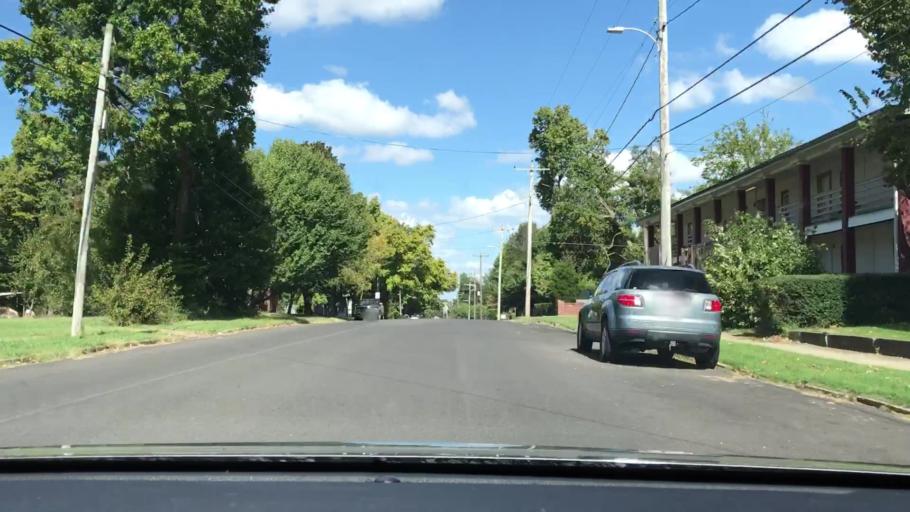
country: US
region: Kentucky
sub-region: Graves County
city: Mayfield
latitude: 36.7435
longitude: -88.6333
